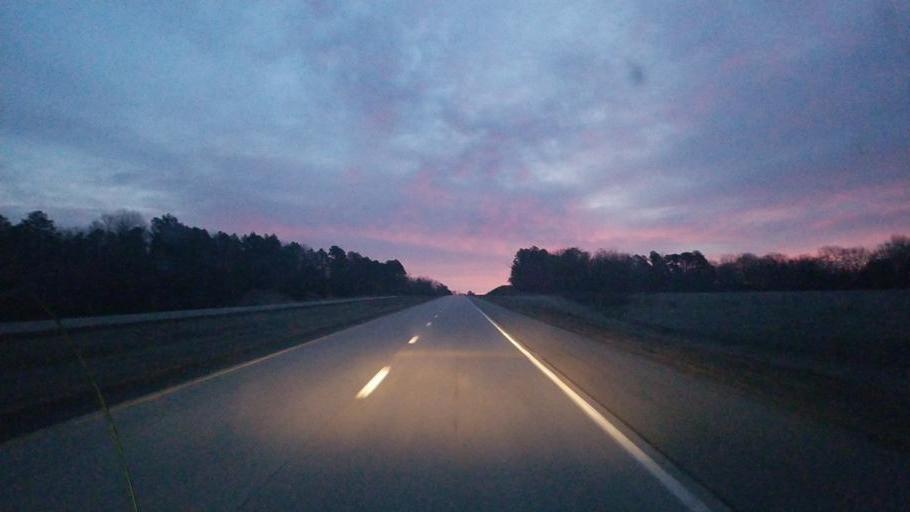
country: US
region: Missouri
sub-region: Shannon County
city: Winona
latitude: 36.9986
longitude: -91.4308
